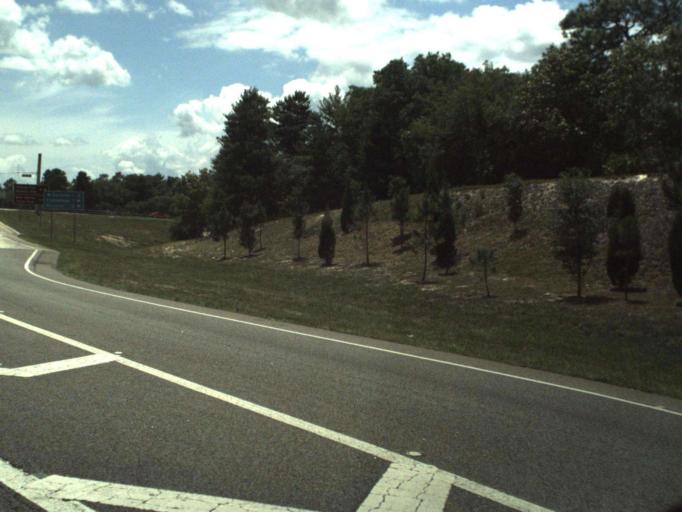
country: US
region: Florida
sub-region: Volusia County
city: Lake Helen
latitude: 28.9575
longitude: -81.2572
